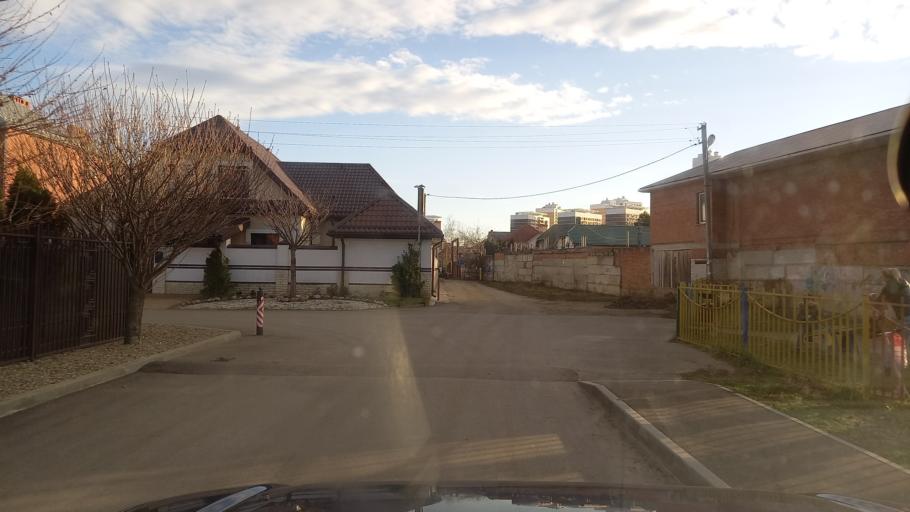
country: RU
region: Krasnodarskiy
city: Pashkovskiy
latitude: 45.0116
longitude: 39.1066
